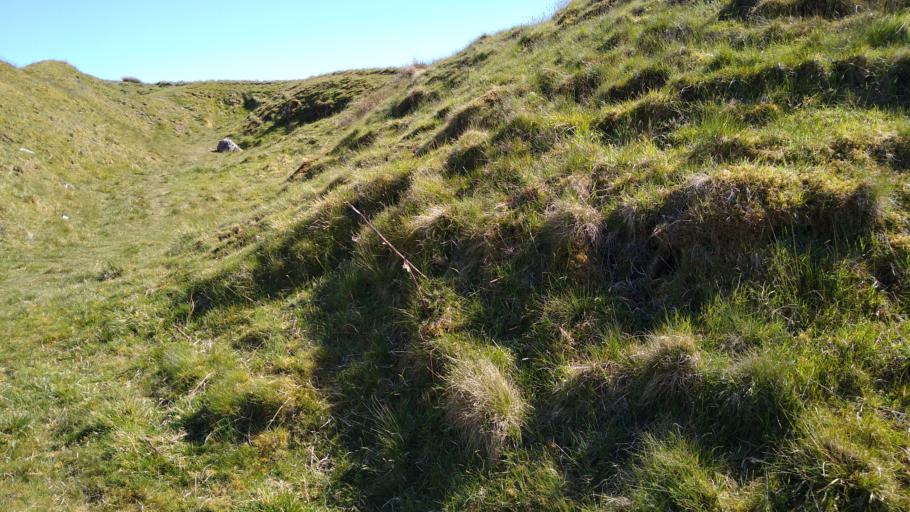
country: GB
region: England
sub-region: Cumbria
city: Wigton
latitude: 54.7591
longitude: -3.0857
